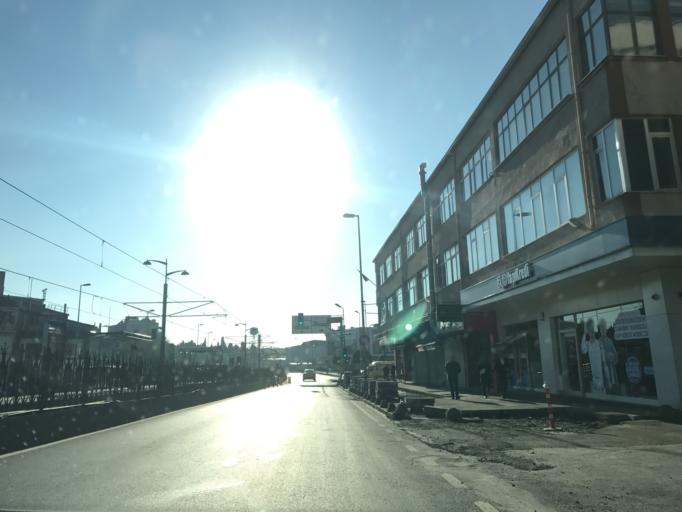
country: TR
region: Istanbul
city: Istanbul
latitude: 41.0371
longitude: 28.9232
